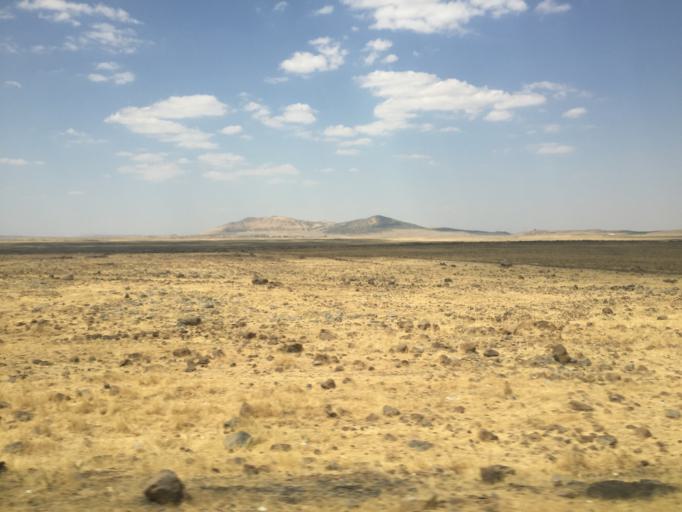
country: TR
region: Sanliurfa
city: Karacadag
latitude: 37.8468
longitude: 39.7095
